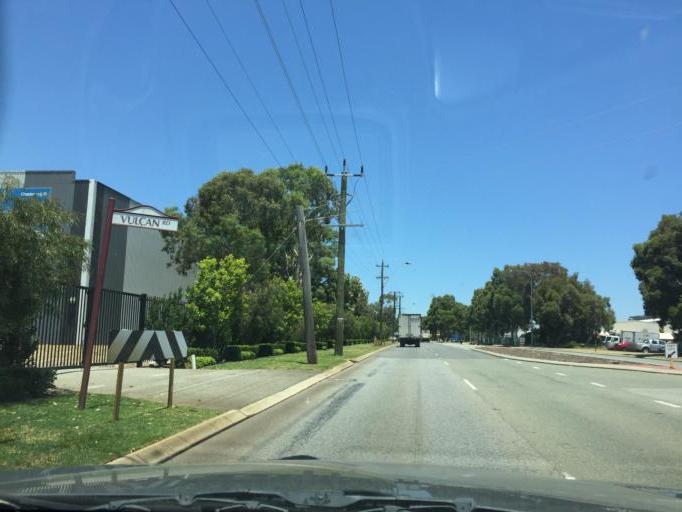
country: AU
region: Western Australia
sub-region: Canning
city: Canning Vale
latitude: -32.0602
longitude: 115.9310
